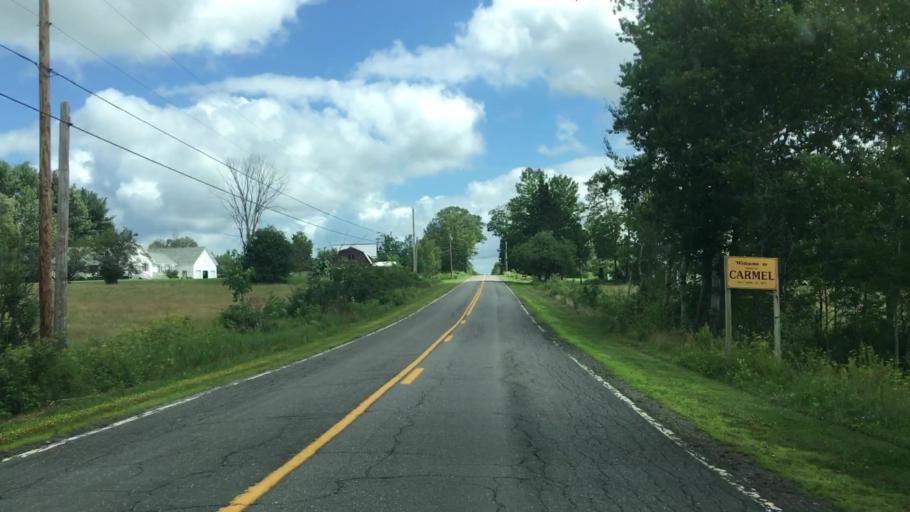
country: US
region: Maine
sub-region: Penobscot County
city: Etna
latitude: 44.7892
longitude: -69.0913
